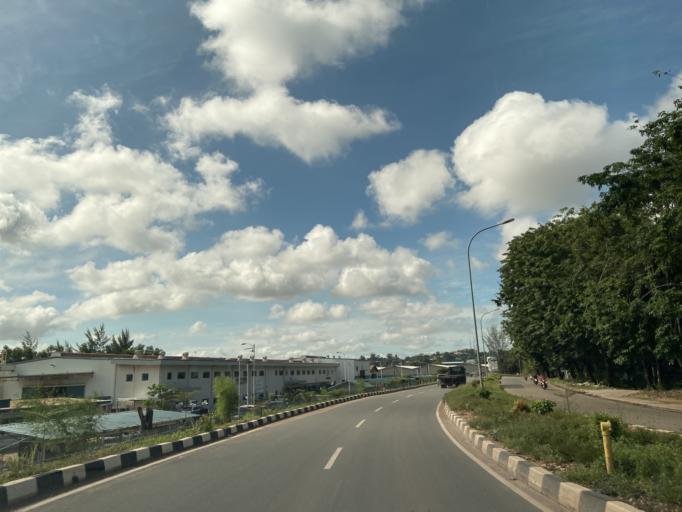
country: SG
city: Singapore
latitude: 1.1734
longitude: 104.0119
